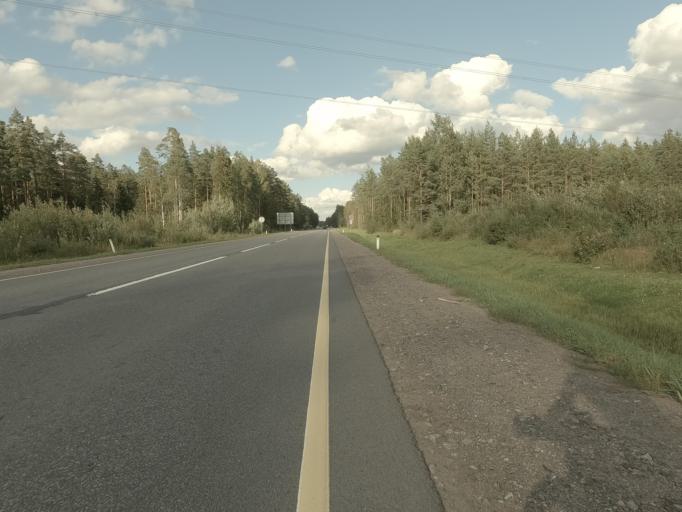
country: RU
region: Leningrad
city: Mga
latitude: 59.7094
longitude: 31.0208
